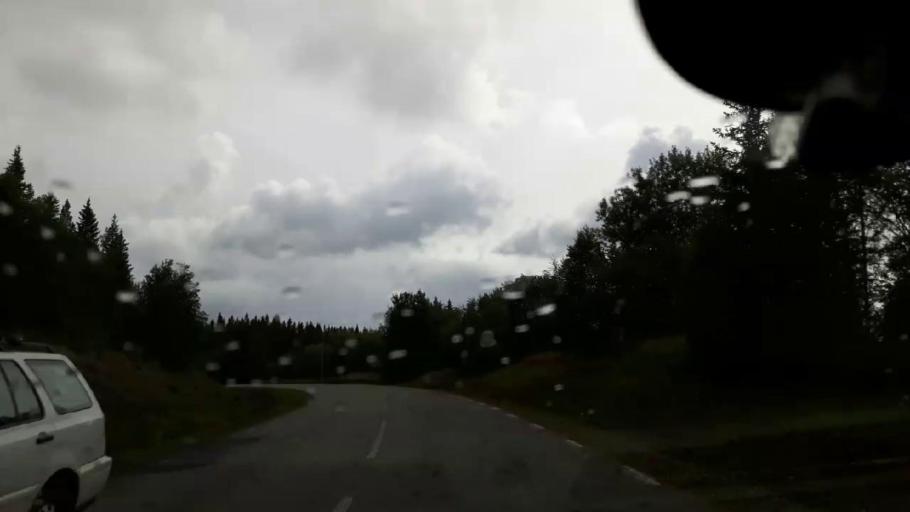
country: SE
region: Jaemtland
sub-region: Krokoms Kommun
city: Valla
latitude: 63.4175
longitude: 13.7941
